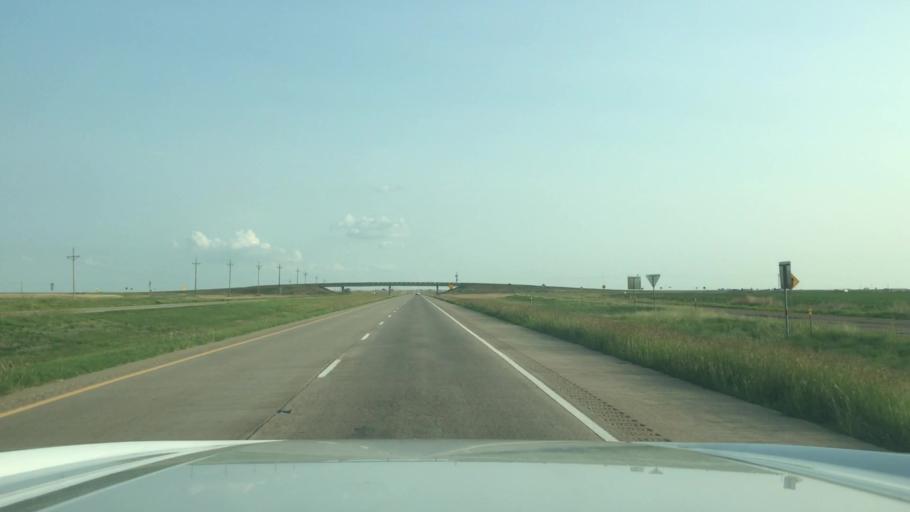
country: US
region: Texas
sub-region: Randall County
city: Canyon
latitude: 34.8428
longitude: -101.8489
